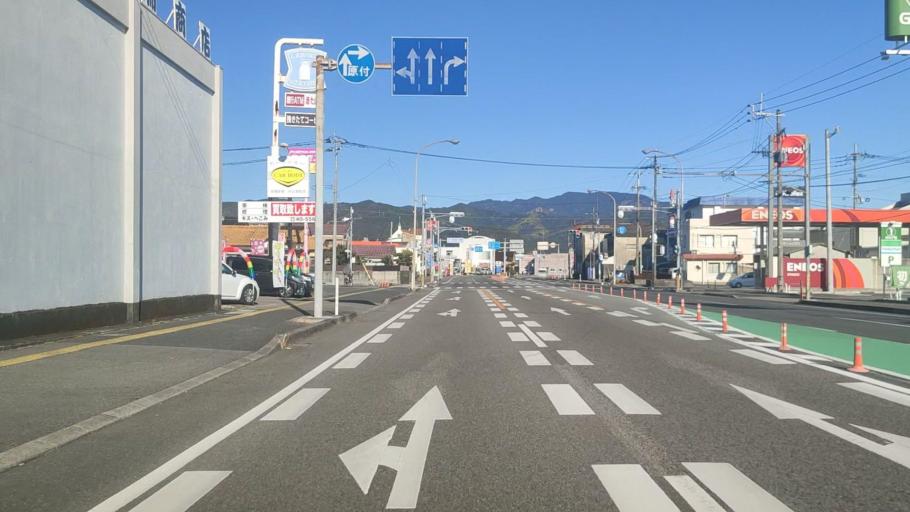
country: JP
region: Miyazaki
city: Nobeoka
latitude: 32.5889
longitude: 131.6762
